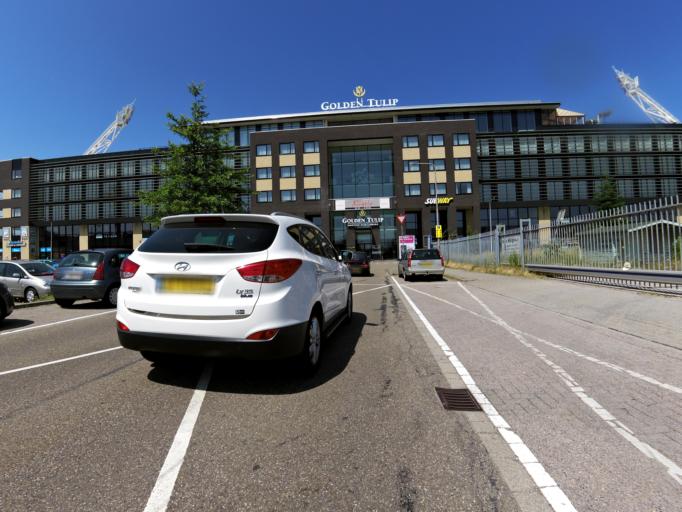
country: NL
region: Limburg
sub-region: Gemeente Simpelveld
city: Simpelveld
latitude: 50.8560
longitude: 6.0067
